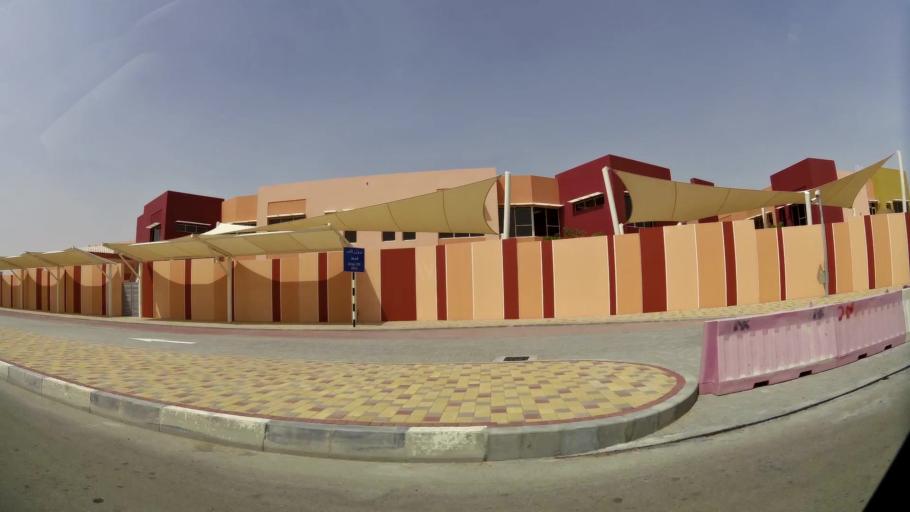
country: AE
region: Abu Dhabi
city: Al Ain
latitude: 24.1598
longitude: 55.6627
